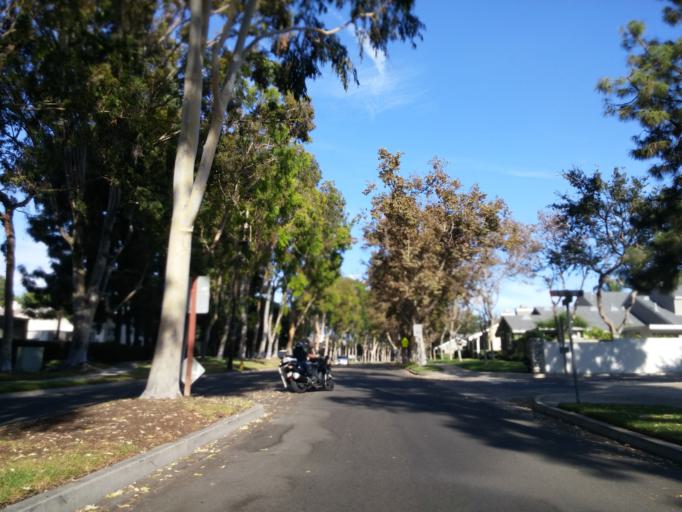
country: US
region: California
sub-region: Orange County
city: Irvine
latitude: 33.6710
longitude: -117.8139
